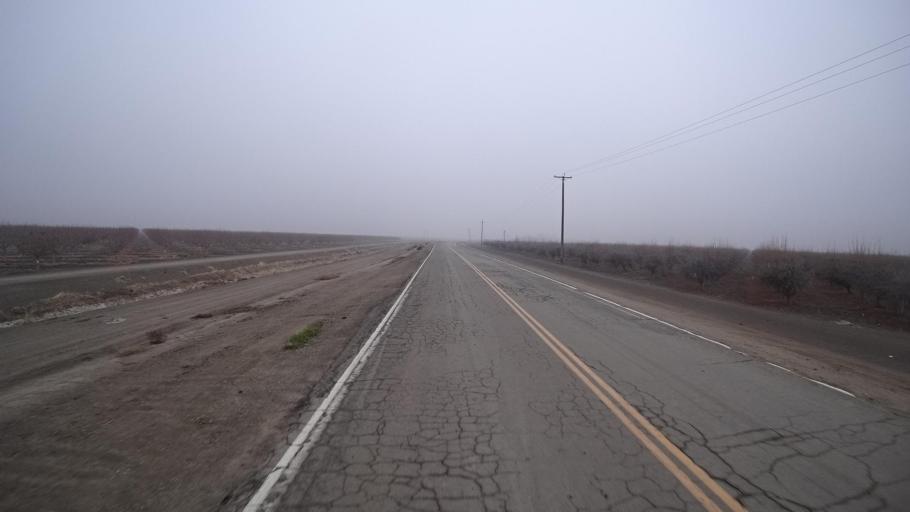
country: US
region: California
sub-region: Kern County
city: Lost Hills
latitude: 35.5058
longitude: -119.6080
